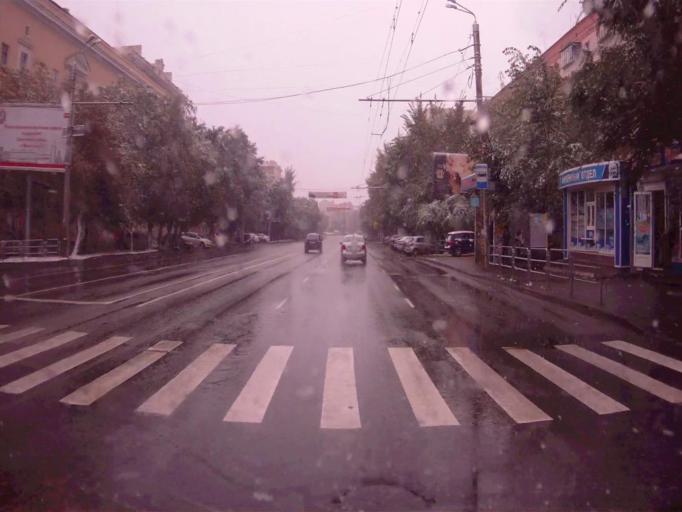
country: RU
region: Chelyabinsk
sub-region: Gorod Chelyabinsk
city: Chelyabinsk
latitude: 55.1502
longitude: 61.4156
